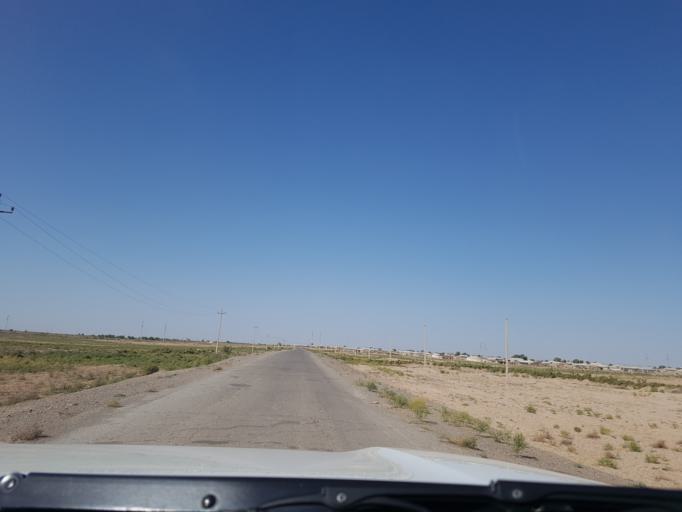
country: IR
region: Razavi Khorasan
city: Sarakhs
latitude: 36.5042
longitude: 61.2535
